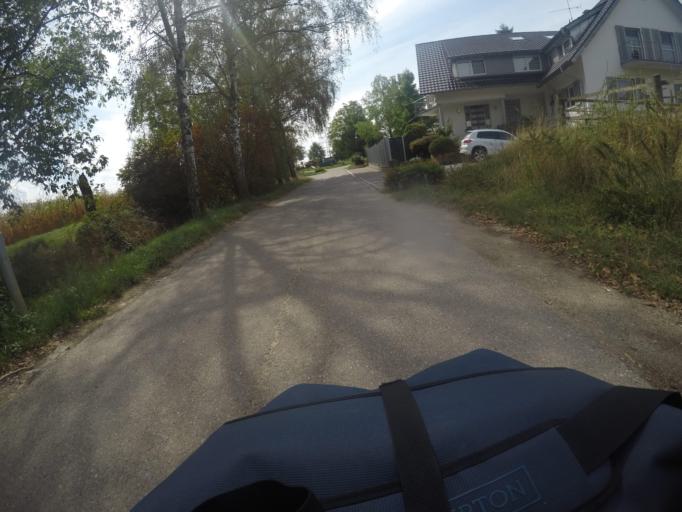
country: DE
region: Baden-Wuerttemberg
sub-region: Freiburg Region
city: Pfaffenweiler
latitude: 47.9167
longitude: 7.7287
